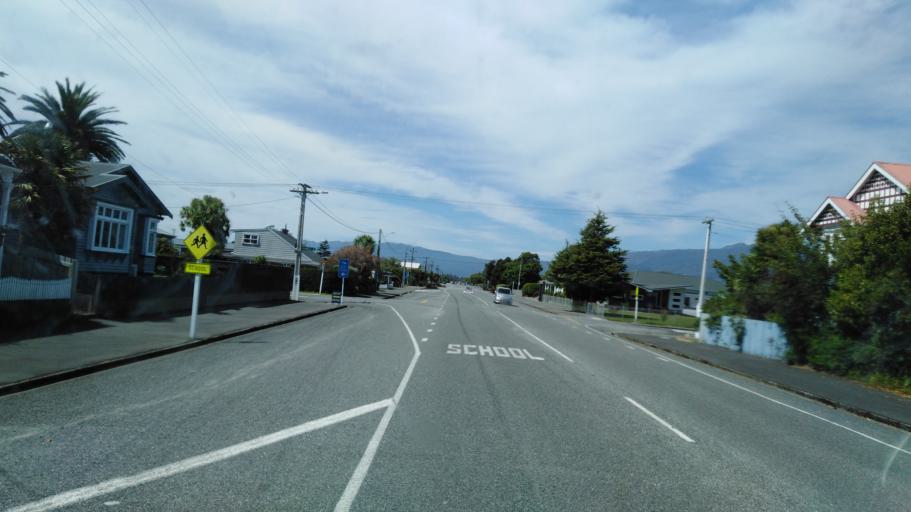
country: NZ
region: West Coast
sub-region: Buller District
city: Westport
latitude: -41.7548
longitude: 171.6038
